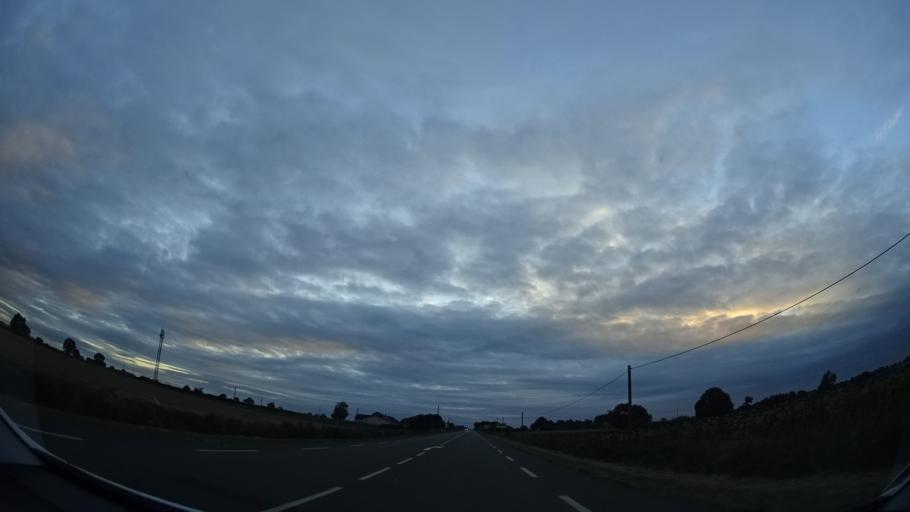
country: FR
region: Pays de la Loire
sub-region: Departement de la Mayenne
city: Sainte-Suzanne
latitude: 48.0329
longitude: -0.3453
